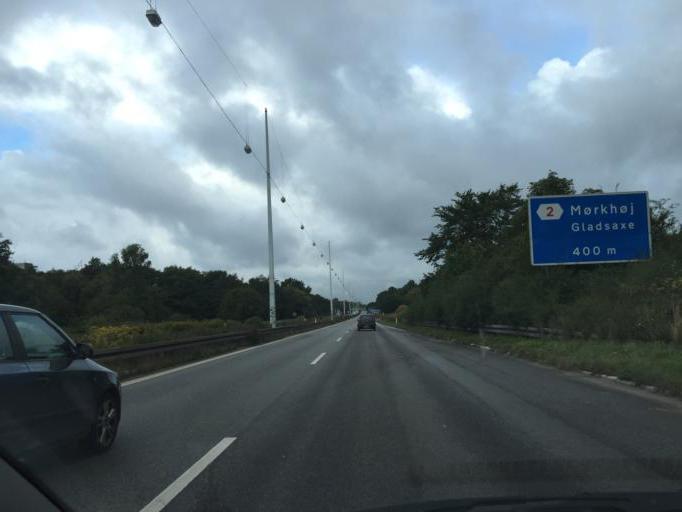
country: DK
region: Capital Region
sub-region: Gladsaxe Municipality
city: Buddinge
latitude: 55.7256
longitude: 12.4855
